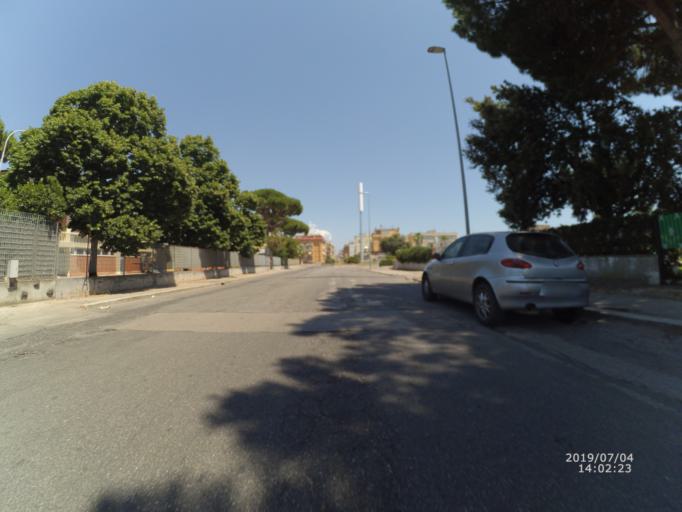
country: IT
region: Latium
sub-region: Provincia di Latina
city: Terracina
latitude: 41.2864
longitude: 13.2347
